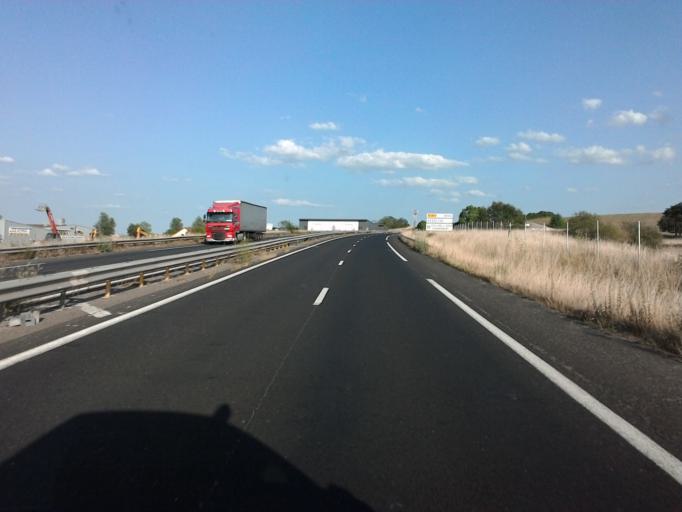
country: FR
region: Lorraine
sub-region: Departement de Meurthe-et-Moselle
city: Flavigny-sur-Moselle
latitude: 48.5602
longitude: 6.1809
